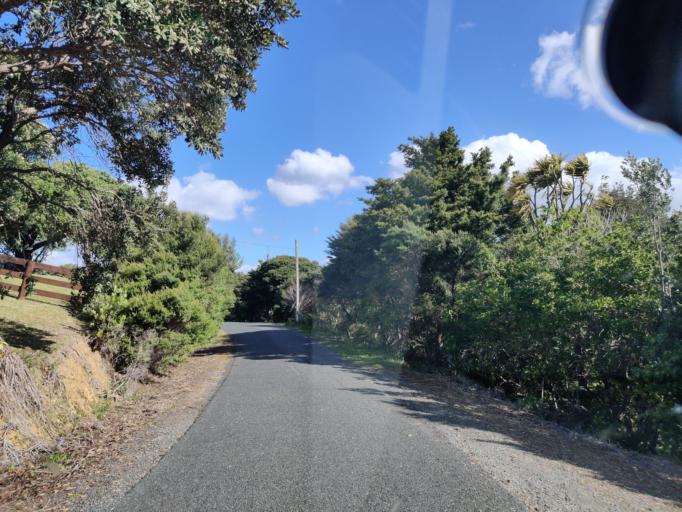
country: NZ
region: Northland
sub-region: Whangarei
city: Ngunguru
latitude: -35.6094
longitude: 174.5295
